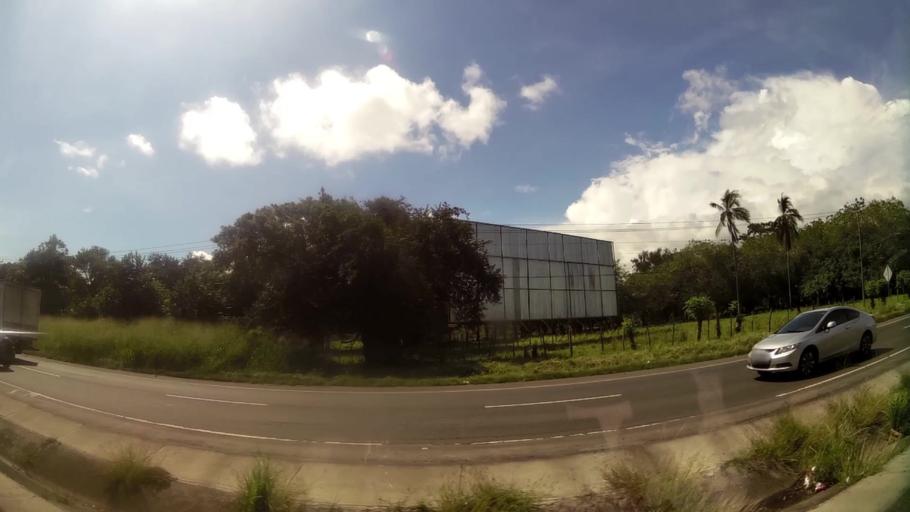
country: PA
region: Panama
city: Bejuco
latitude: 8.6164
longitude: -79.8809
